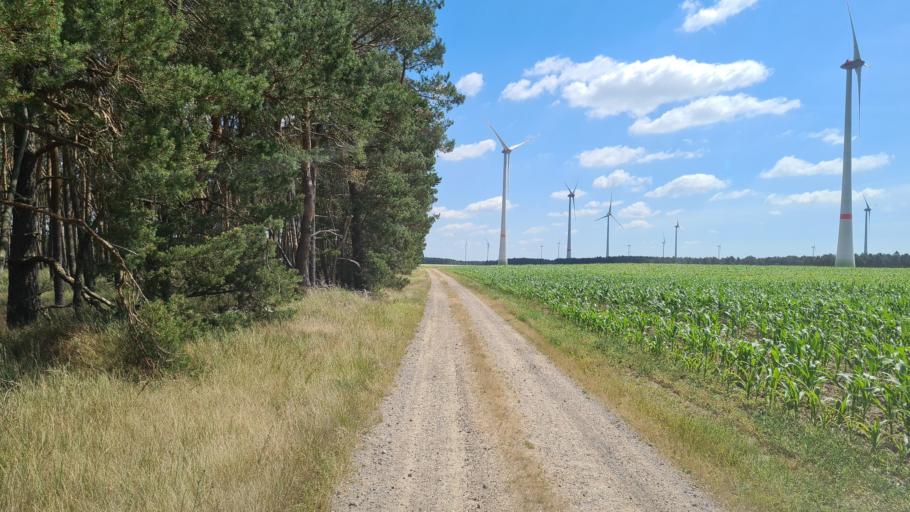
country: DE
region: Brandenburg
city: Treuenbrietzen
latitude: 52.0317
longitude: 12.8495
